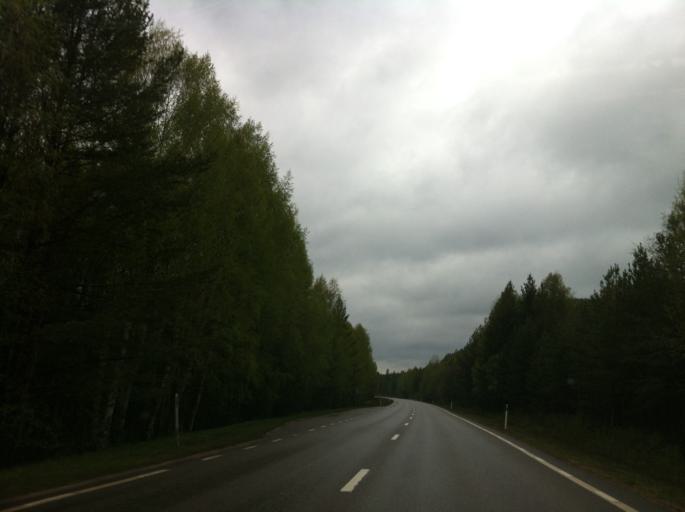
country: SE
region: Jaemtland
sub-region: Harjedalens Kommun
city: Sveg
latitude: 62.0965
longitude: 14.2324
